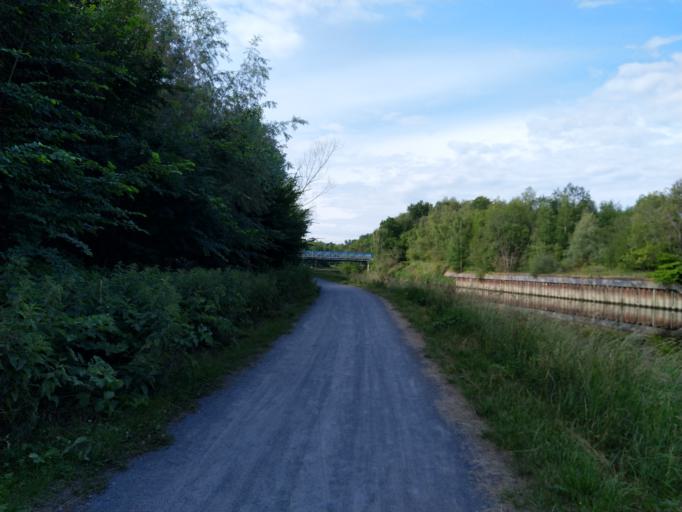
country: FR
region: Nord-Pas-de-Calais
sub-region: Departement du Nord
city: Recquignies
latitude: 50.2843
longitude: 4.0359
